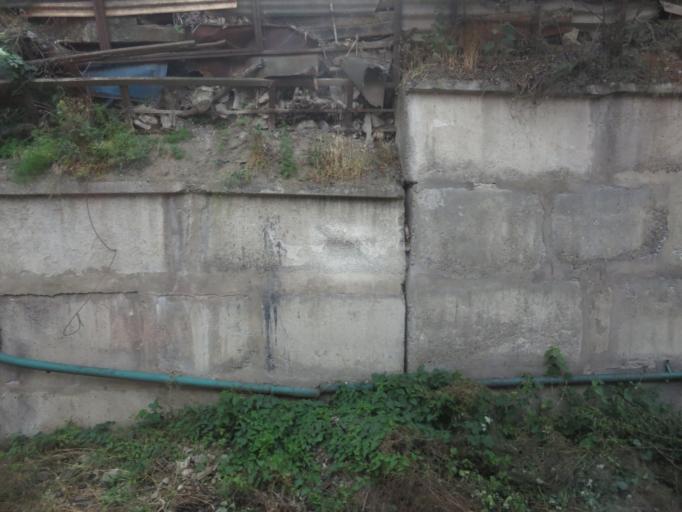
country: GE
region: Mtskheta-Mtianeti
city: Mtskheta
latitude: 41.8374
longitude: 44.7054
